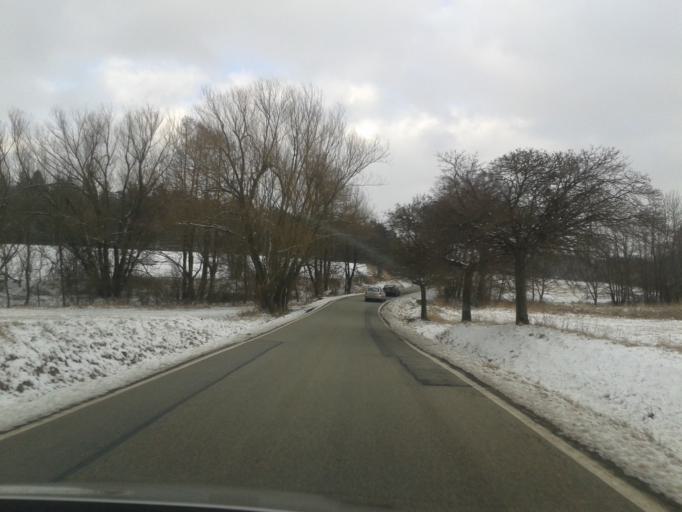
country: CZ
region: Olomoucky
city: Konice
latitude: 49.5879
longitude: 16.8370
